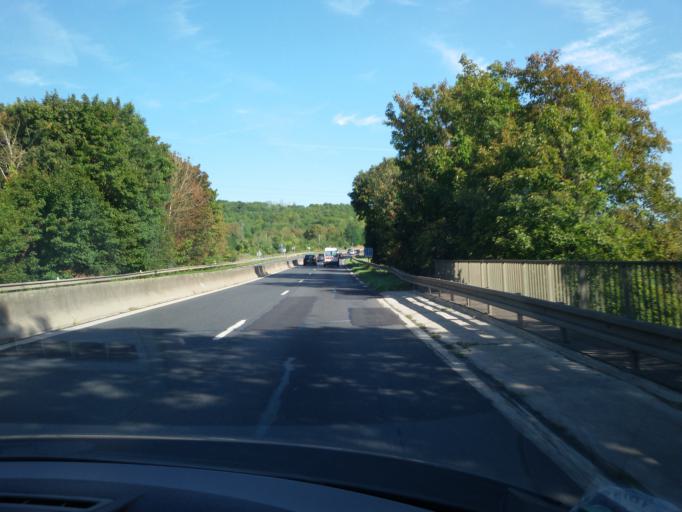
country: FR
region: Ile-de-France
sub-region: Departement de l'Essonne
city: Etrechy
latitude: 48.5025
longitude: 2.2009
